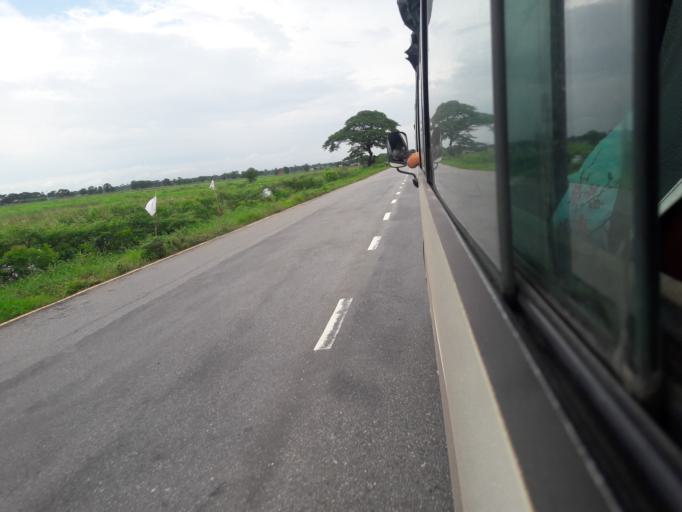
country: MM
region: Bago
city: Nyaunglebin
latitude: 17.8427
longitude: 96.6875
